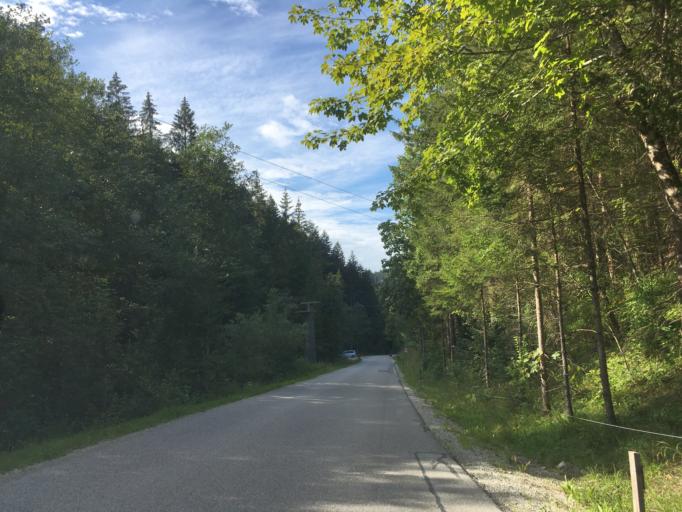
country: AT
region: Salzburg
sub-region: Politischer Bezirk Sankt Johann im Pongau
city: Filzmoos
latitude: 47.5191
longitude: 13.4490
